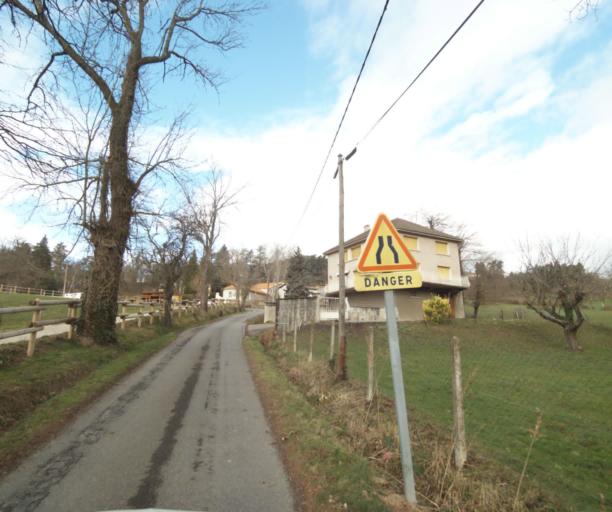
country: FR
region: Rhone-Alpes
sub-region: Departement de la Loire
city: La Talaudiere
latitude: 45.4806
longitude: 4.4124
